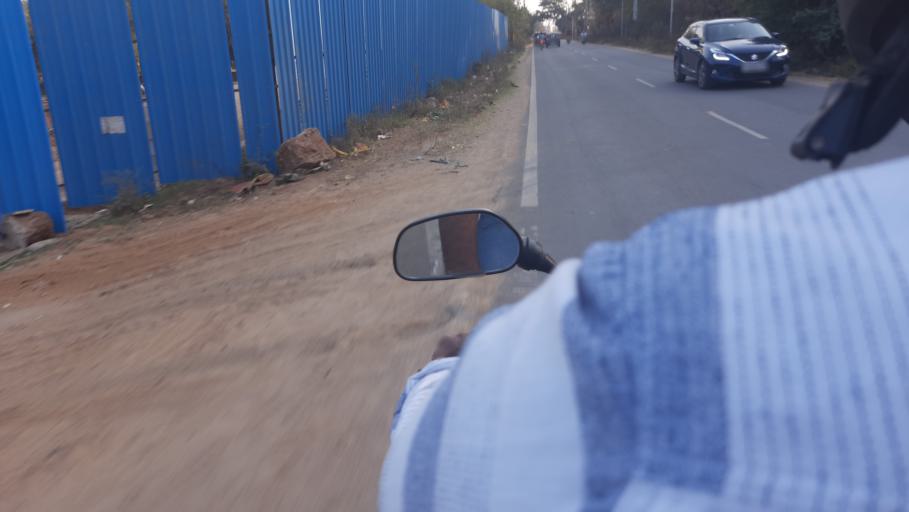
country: IN
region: Telangana
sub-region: Rangareddi
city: Secunderabad
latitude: 17.5151
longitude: 78.5401
